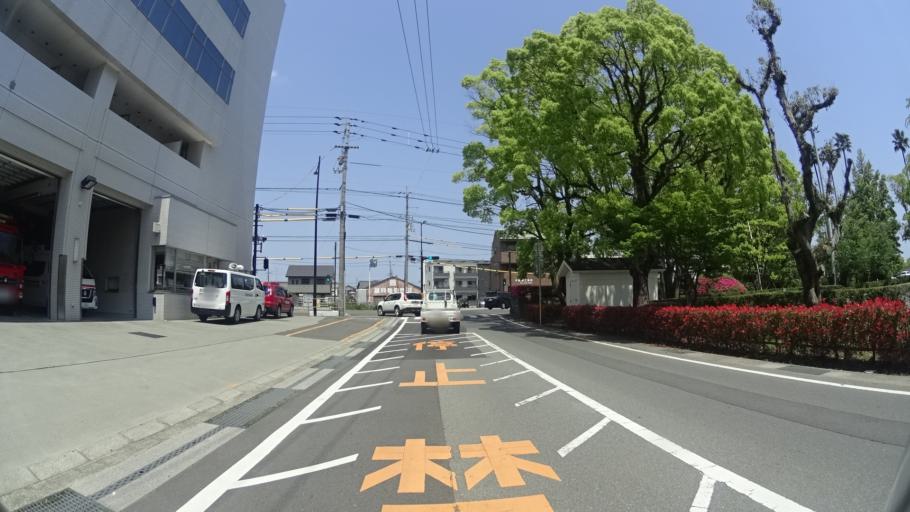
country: JP
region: Tokushima
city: Tokushima-shi
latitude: 34.0747
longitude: 134.5125
